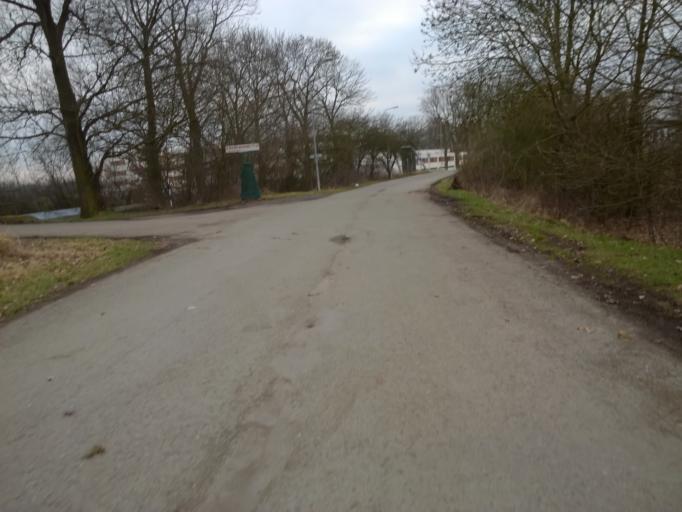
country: CZ
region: Pardubicky
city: Stare Hradiste
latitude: 50.0558
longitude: 15.7733
